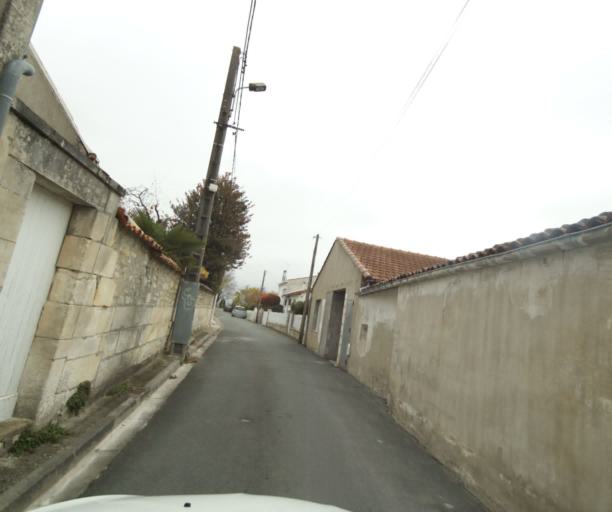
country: FR
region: Poitou-Charentes
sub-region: Departement de la Charente-Maritime
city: Saintes
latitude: 45.7504
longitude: -0.6387
